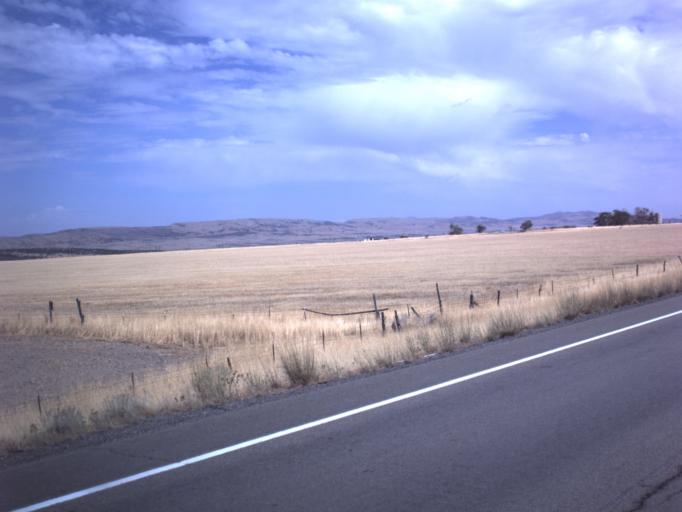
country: US
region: Utah
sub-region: Juab County
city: Nephi
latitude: 39.4364
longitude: -111.9164
